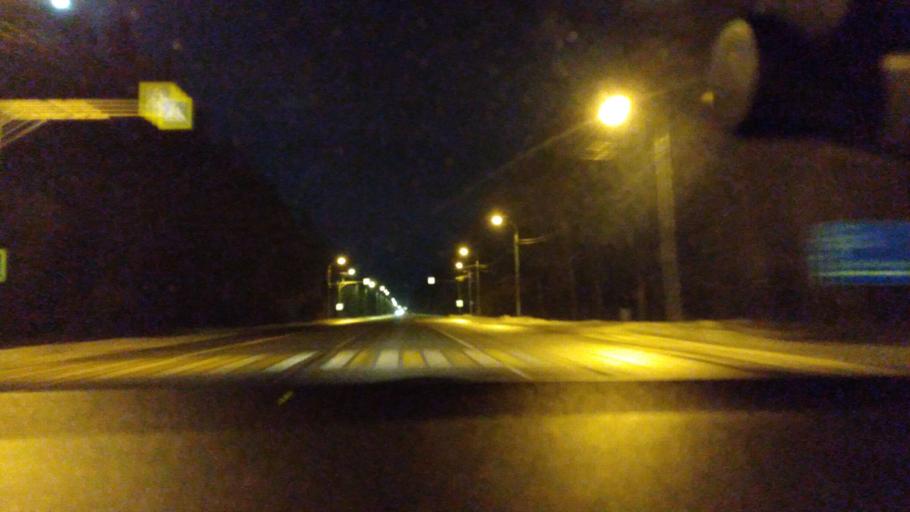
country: RU
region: Moskovskaya
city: Il'inskiy Pogost
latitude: 55.4595
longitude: 38.9857
